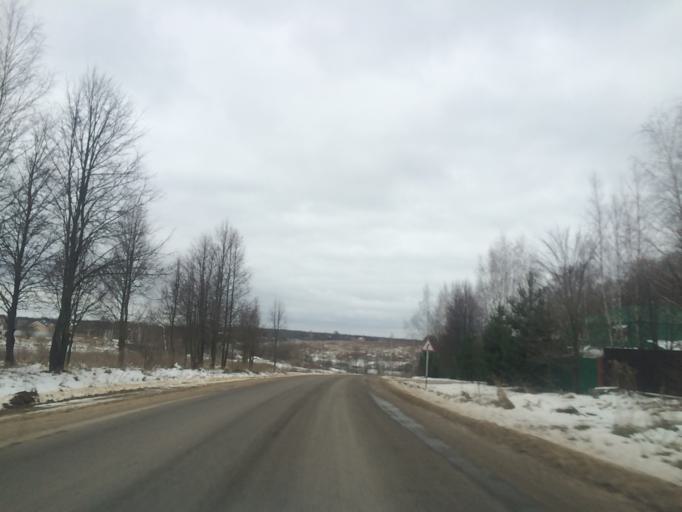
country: RU
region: Tula
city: Kosaya Gora
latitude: 54.1621
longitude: 37.4420
